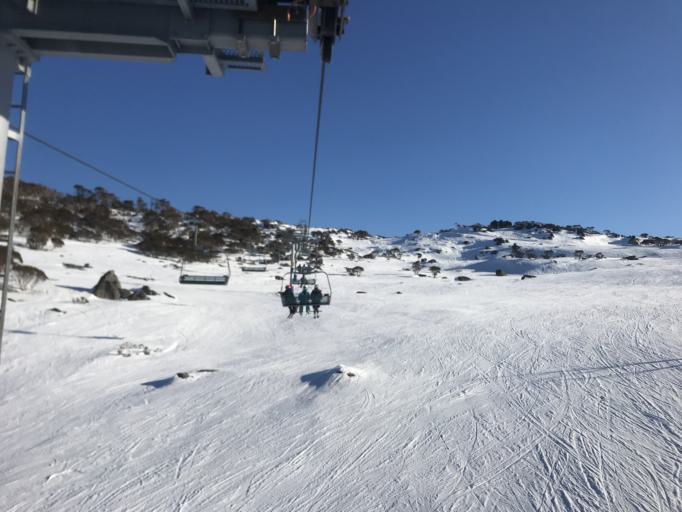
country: AU
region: New South Wales
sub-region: Snowy River
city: Jindabyne
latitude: -36.3901
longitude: 148.3963
